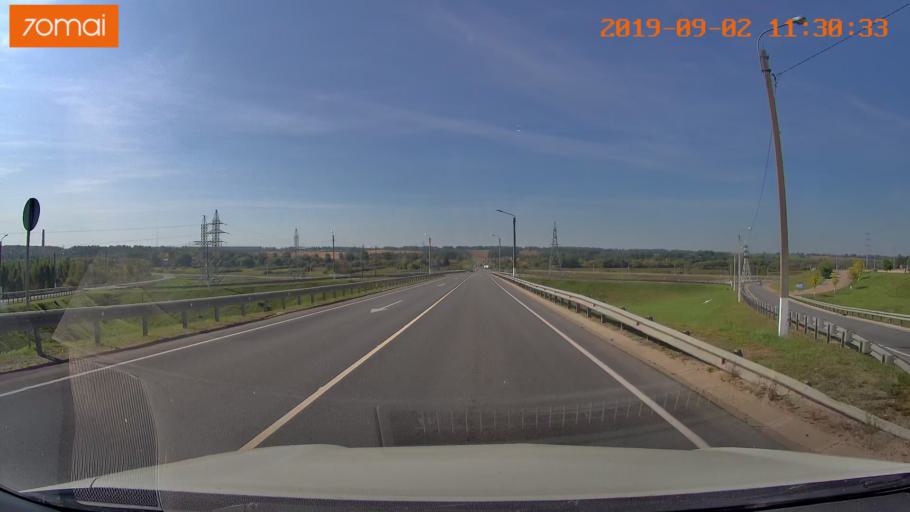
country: RU
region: Smolensk
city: Roslavl'
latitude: 53.9830
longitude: 32.8316
